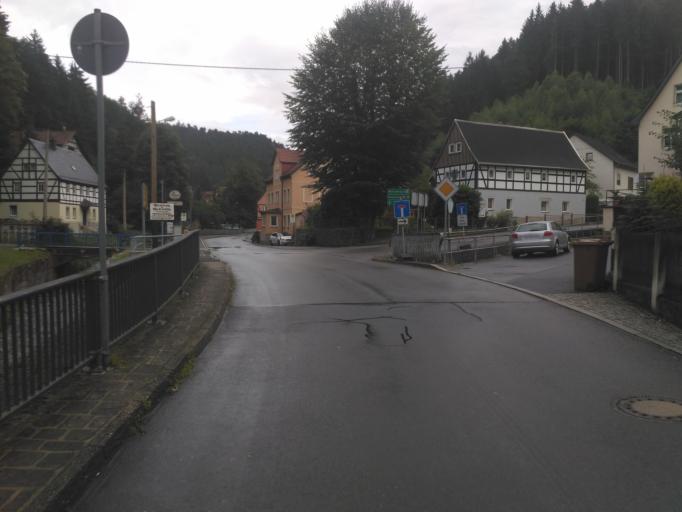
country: DE
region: Saxony
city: Bad Schandau
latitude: 50.9047
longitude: 14.1638
